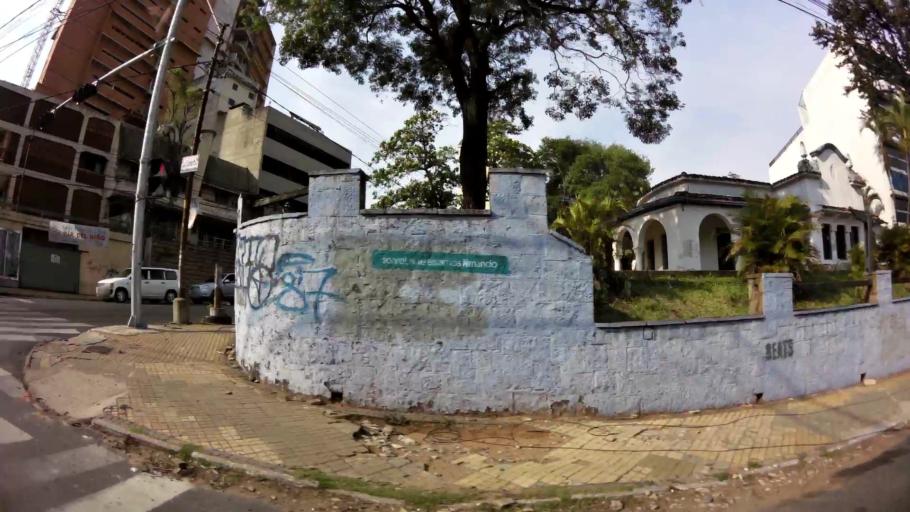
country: PY
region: Asuncion
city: Asuncion
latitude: -25.2862
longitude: -57.6169
